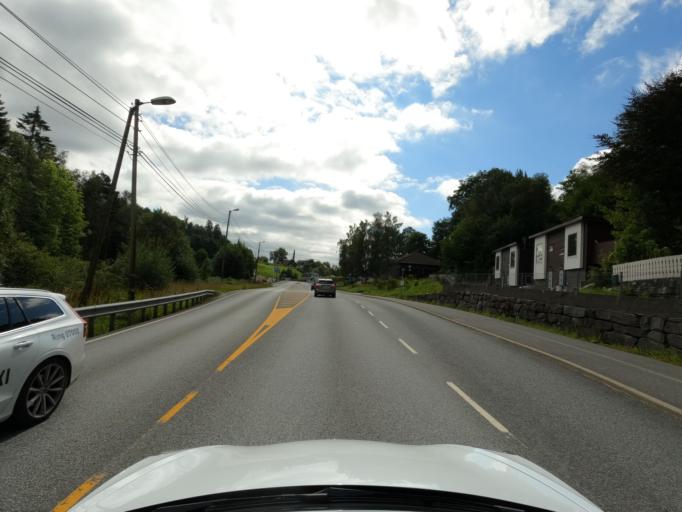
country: NO
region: Hordaland
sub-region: Os
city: Osoyro
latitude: 60.1939
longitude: 5.4630
